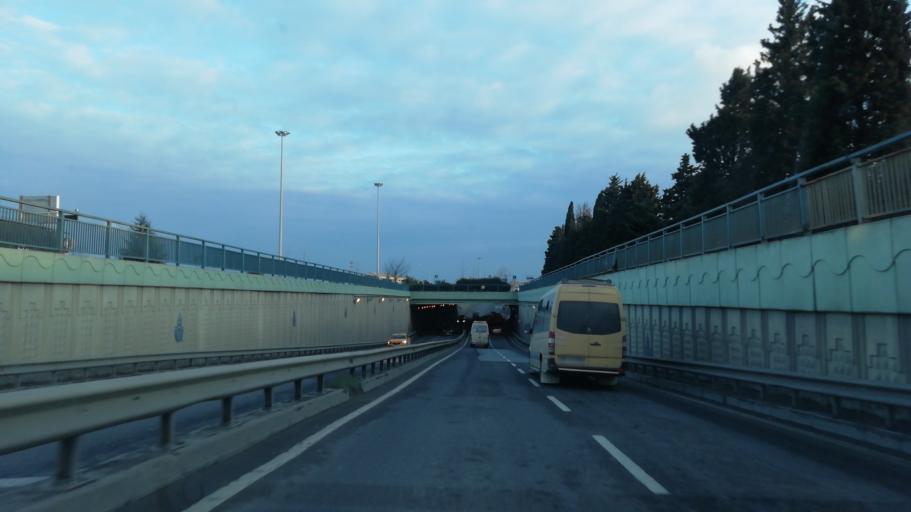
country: TR
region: Istanbul
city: Yakuplu
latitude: 40.9896
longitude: 28.7202
